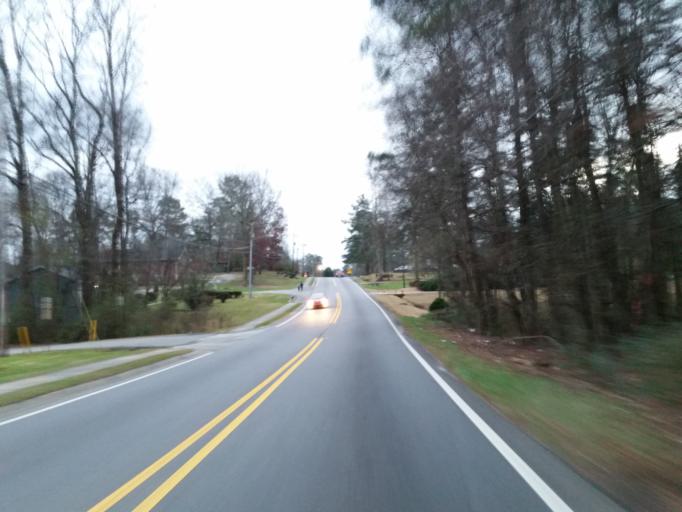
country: US
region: Georgia
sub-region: Cobb County
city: Fair Oaks
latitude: 33.8794
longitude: -84.5798
